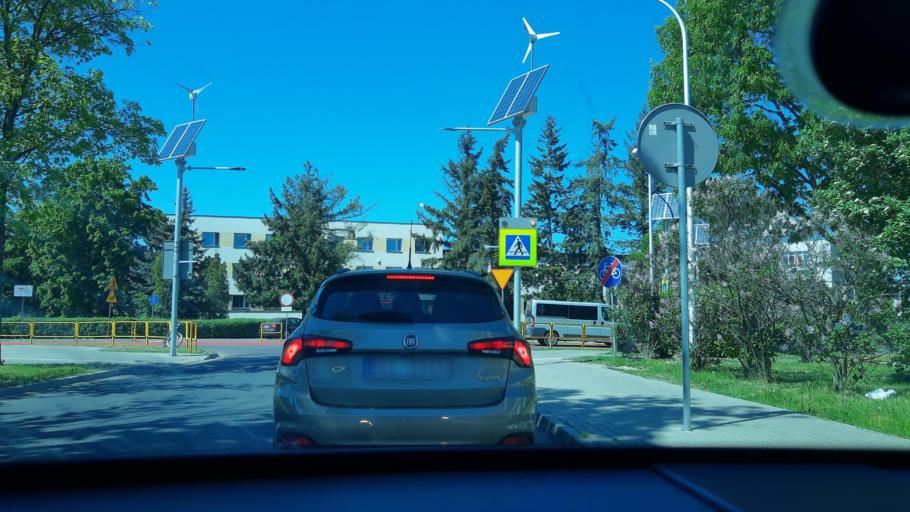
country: PL
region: Lodz Voivodeship
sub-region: Powiat sieradzki
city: Sieradz
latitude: 51.5922
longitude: 18.7324
